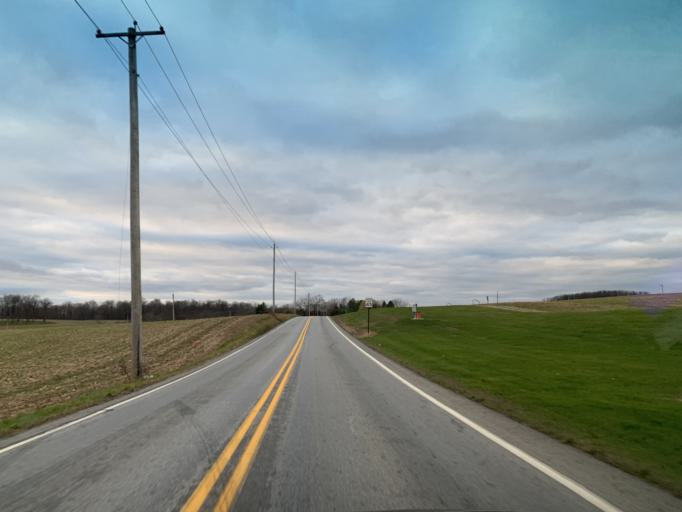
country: US
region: Pennsylvania
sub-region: York County
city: Stewartstown
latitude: 39.7748
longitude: -76.6019
